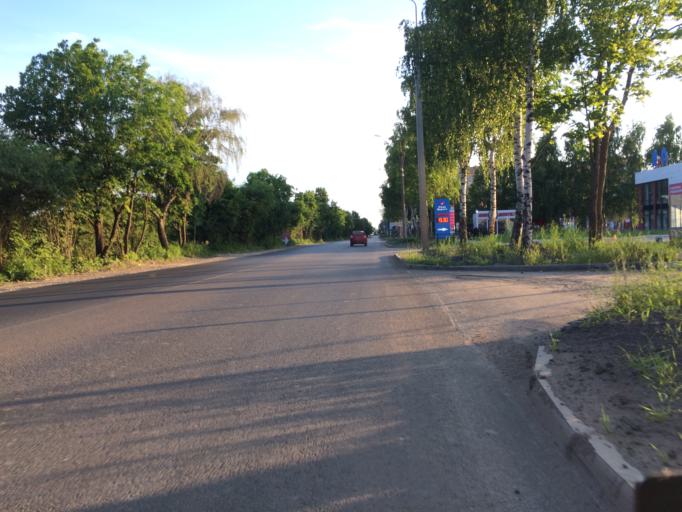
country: RU
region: Mariy-El
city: Medvedevo
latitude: 56.6421
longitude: 47.8317
